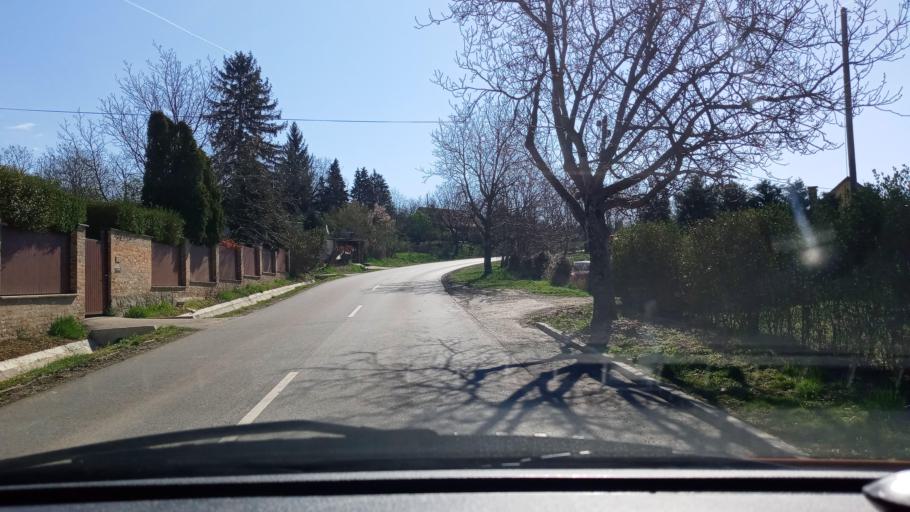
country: HU
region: Baranya
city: Pecs
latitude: 46.0865
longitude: 18.2878
